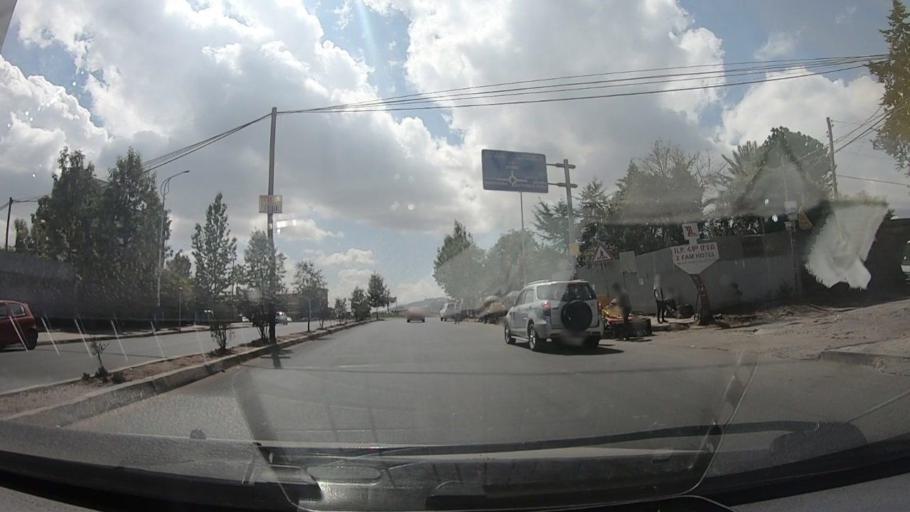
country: ET
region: Adis Abeba
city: Addis Ababa
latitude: 8.9794
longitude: 38.7224
